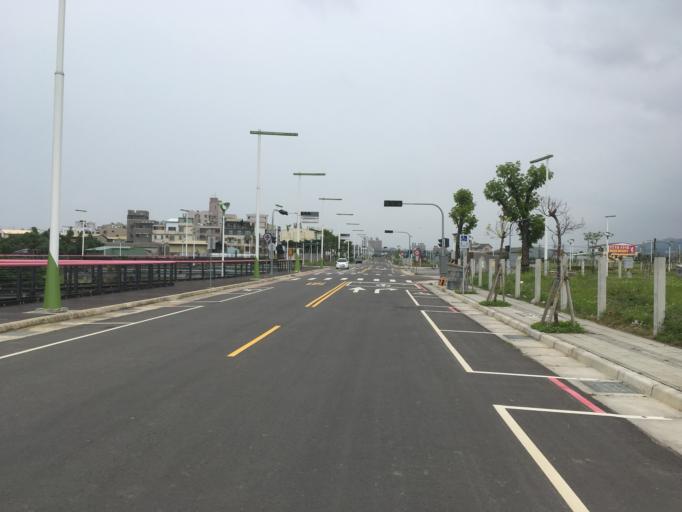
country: TW
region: Taiwan
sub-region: Taichung City
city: Taichung
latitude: 24.1887
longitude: 120.7051
